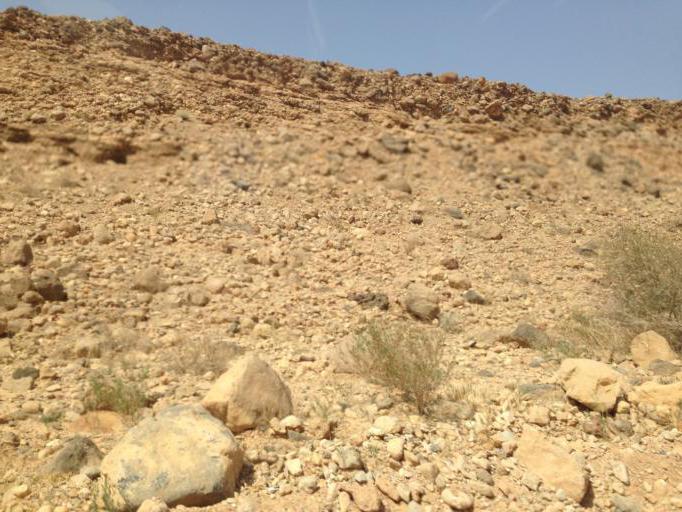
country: OM
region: Ash Sharqiyah
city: Ibra'
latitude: 23.0756
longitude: 58.8776
